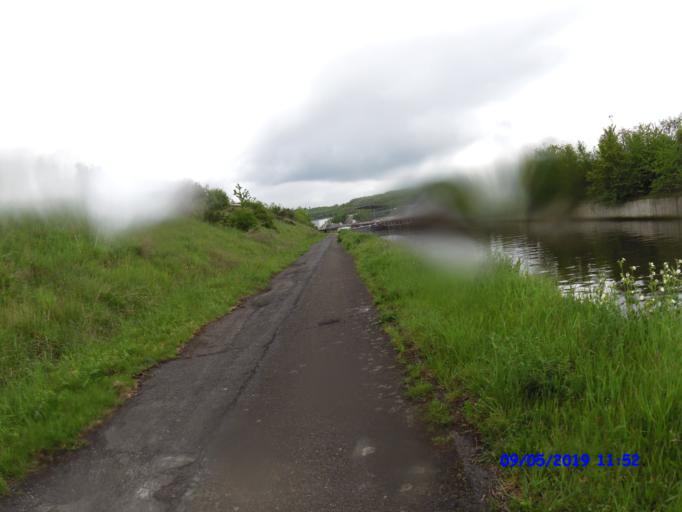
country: BE
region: Wallonia
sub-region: Province du Hainaut
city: Charleroi
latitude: 50.3992
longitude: 4.4660
